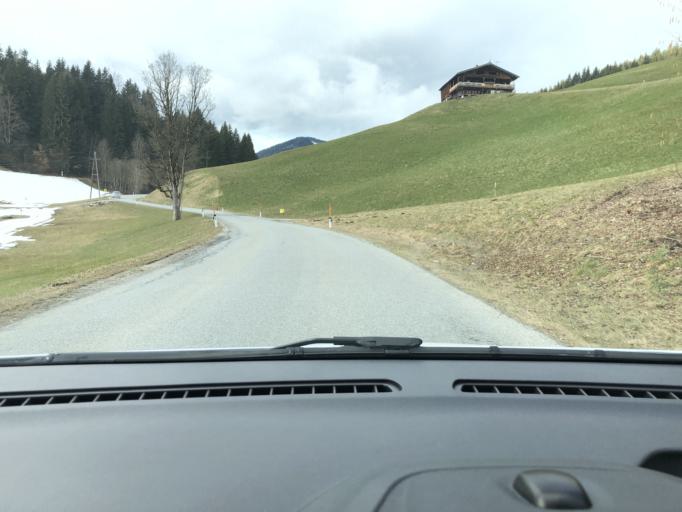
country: AT
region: Tyrol
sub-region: Politischer Bezirk Kitzbuhel
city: Itter
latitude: 47.4494
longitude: 12.1197
